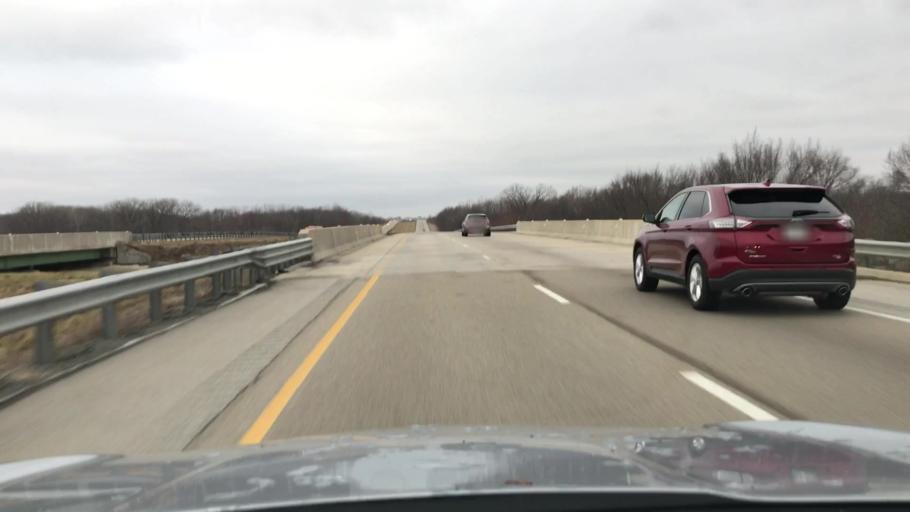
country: US
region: Illinois
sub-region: Logan County
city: Lincoln
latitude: 40.1818
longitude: -89.3631
